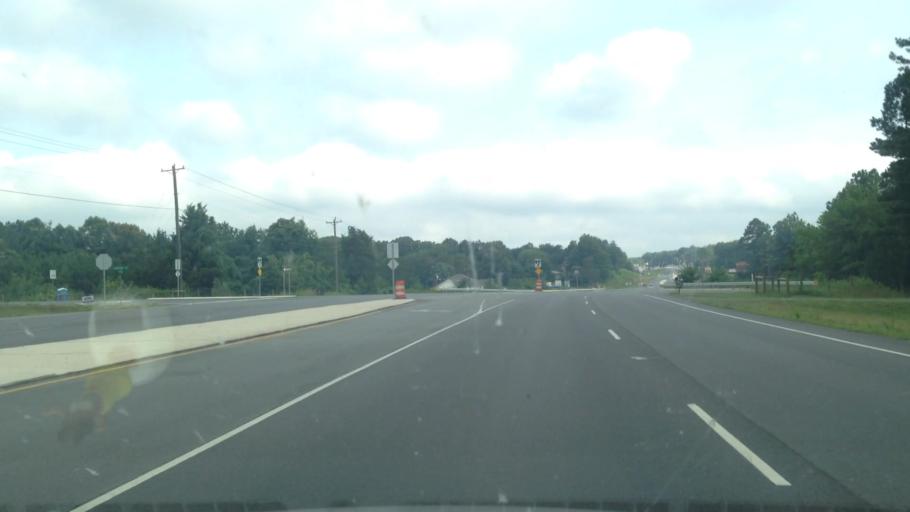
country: US
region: North Carolina
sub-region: Guilford County
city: Summerfield
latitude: 36.1830
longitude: -79.8878
